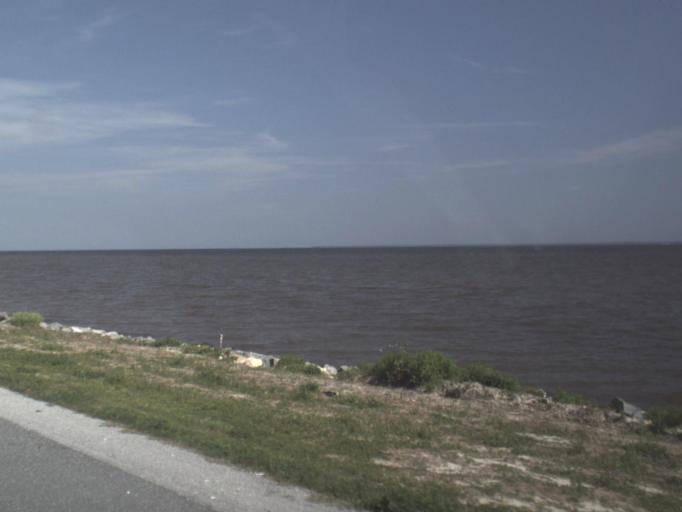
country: US
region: Florida
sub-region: Franklin County
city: Eastpoint
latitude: 29.7481
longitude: -84.8551
